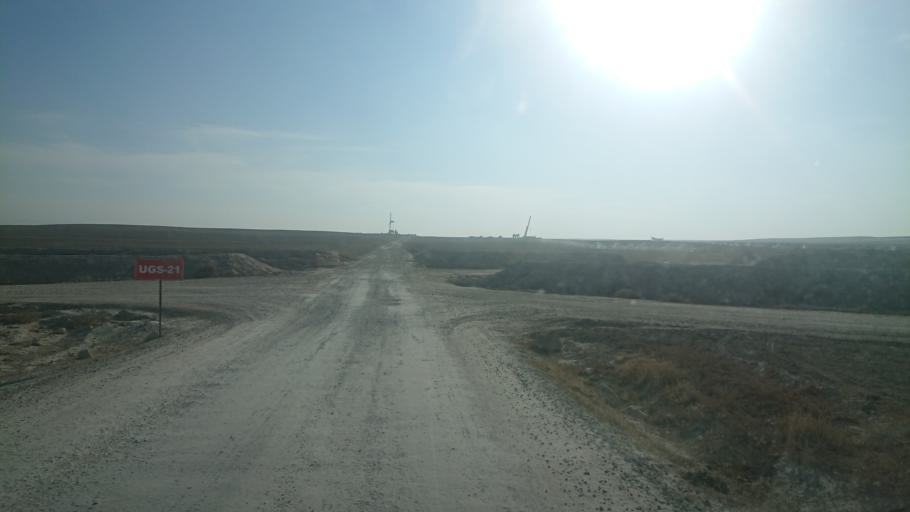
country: TR
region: Aksaray
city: Sultanhani
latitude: 38.0684
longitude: 33.6161
